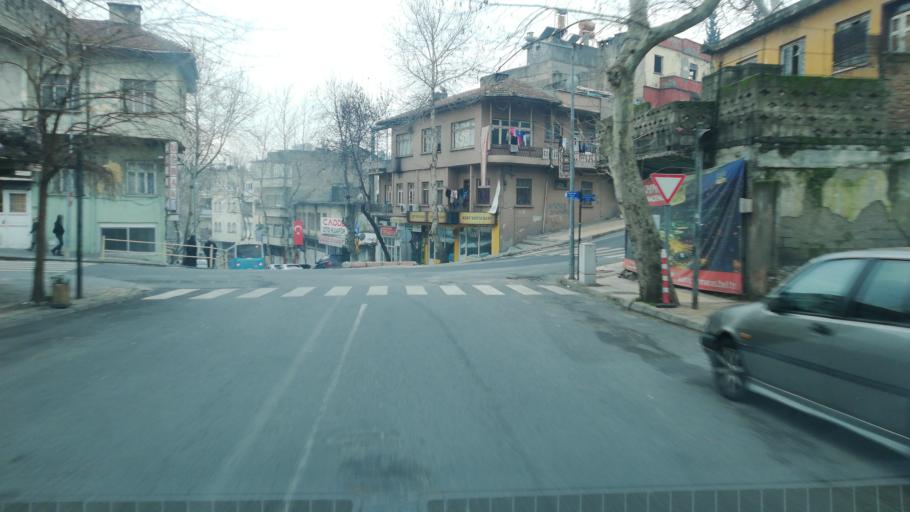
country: TR
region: Kahramanmaras
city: Kahramanmaras
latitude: 37.5902
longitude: 36.9270
